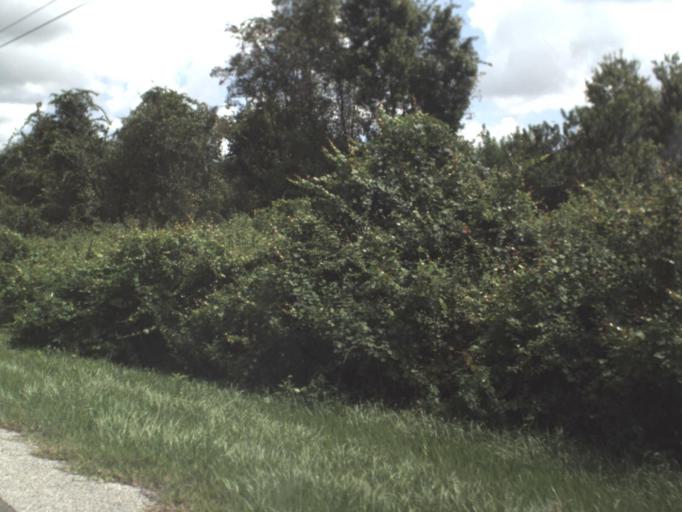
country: US
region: Florida
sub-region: DeSoto County
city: Arcadia
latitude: 27.3436
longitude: -81.8043
